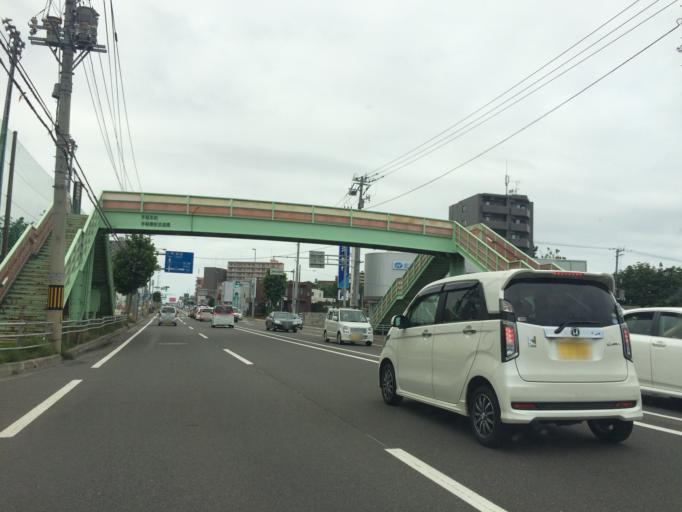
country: JP
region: Hokkaido
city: Sapporo
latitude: 43.1162
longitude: 141.2427
